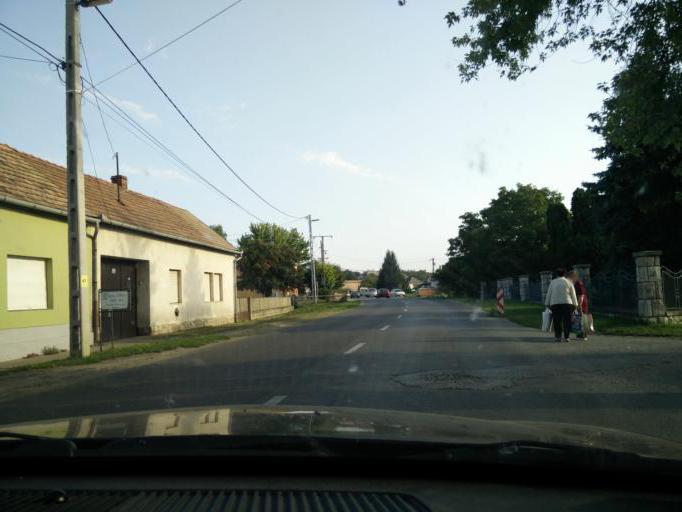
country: HU
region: Baranya
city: Szaszvar
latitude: 46.2753
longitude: 18.3765
